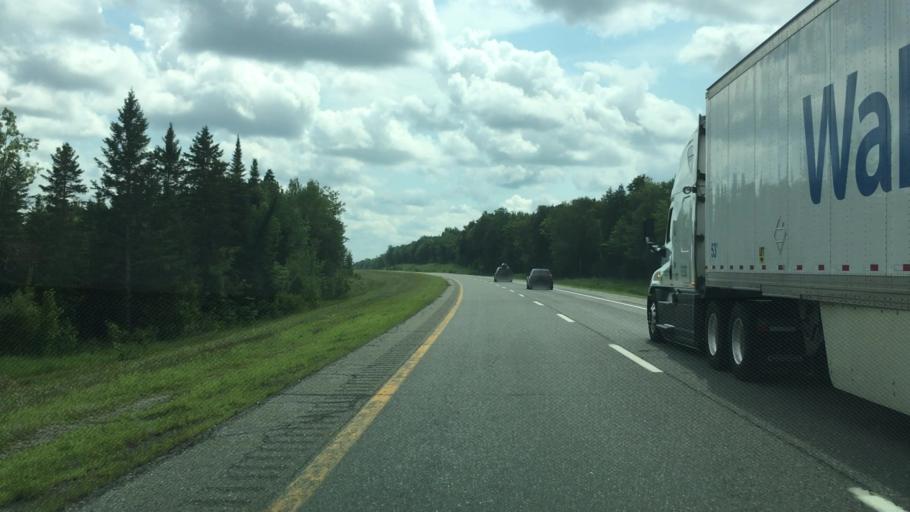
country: US
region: Maine
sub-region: Penobscot County
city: Howland
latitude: 45.3132
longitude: -68.6581
